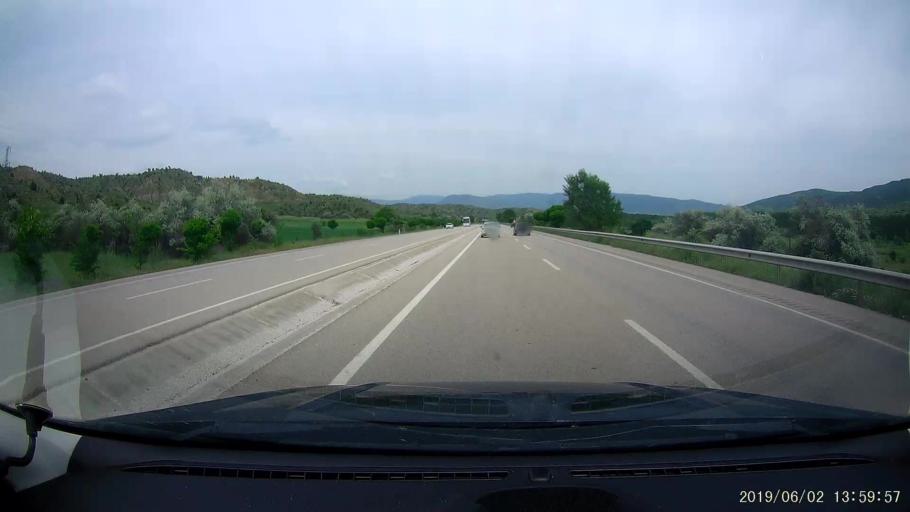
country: TR
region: Cankiri
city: Beloren
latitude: 40.9000
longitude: 33.5554
